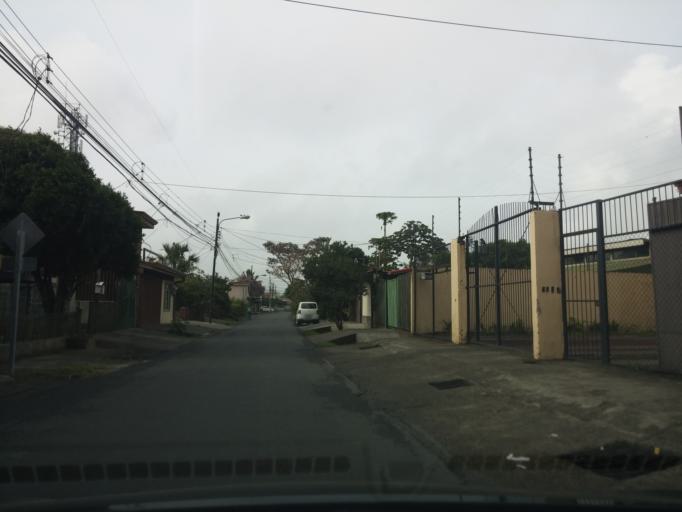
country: CR
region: Heredia
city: Llorente
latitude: 10.0077
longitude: -84.1477
